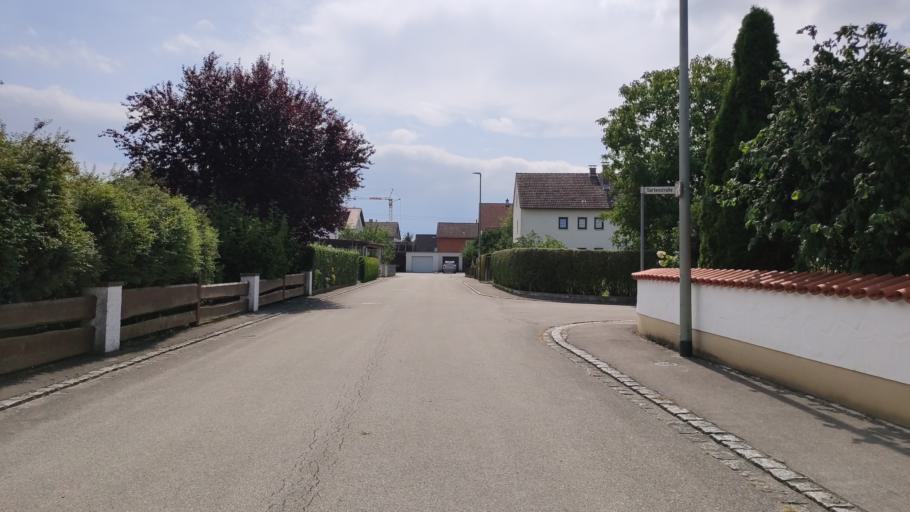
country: DE
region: Bavaria
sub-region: Swabia
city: Oberottmarshausen
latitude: 48.2356
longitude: 10.8598
